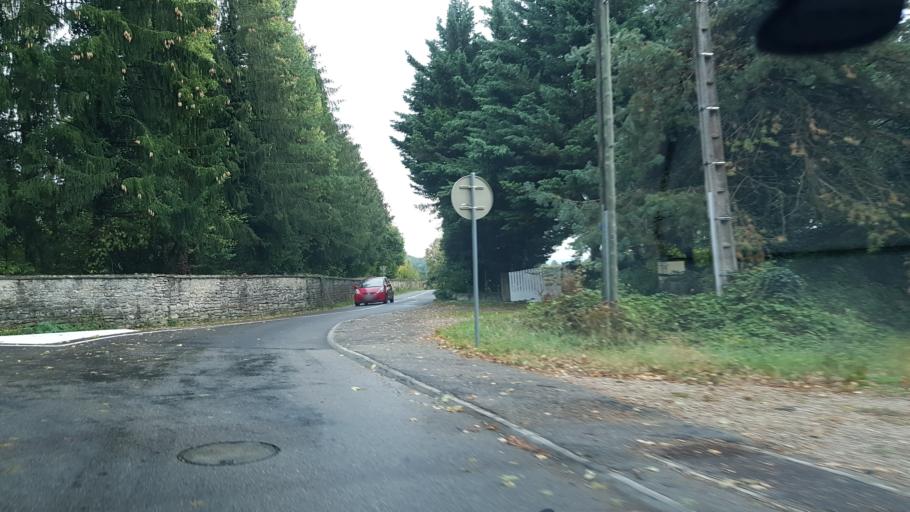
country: FR
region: Rhone-Alpes
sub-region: Departement de l'Ain
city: Ceyzeriat
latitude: 46.1606
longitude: 5.3278
